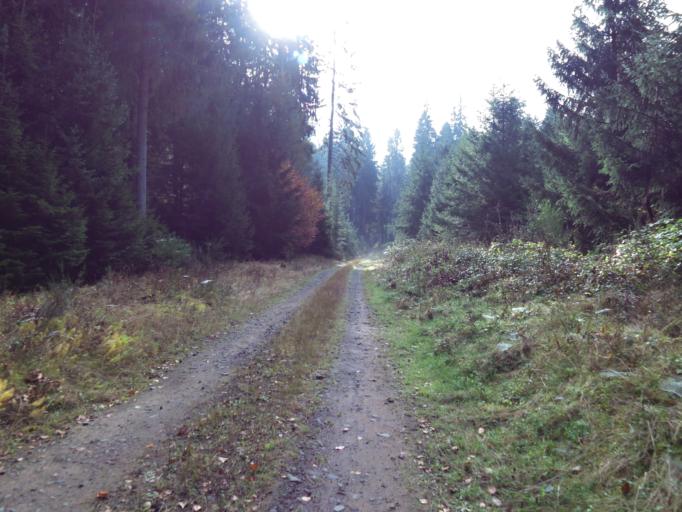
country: DE
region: Rheinland-Pfalz
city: Fischbach
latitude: 49.4809
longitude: 7.9513
